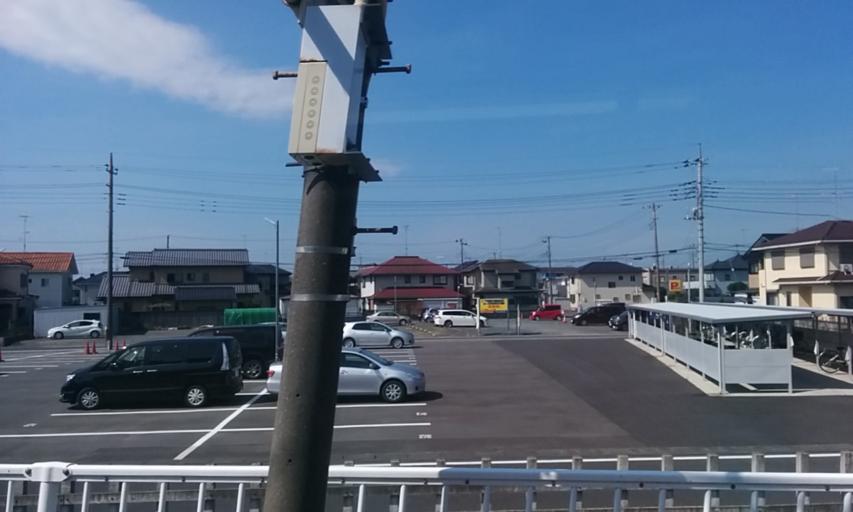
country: JP
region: Saitama
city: Hanyu
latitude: 36.1495
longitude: 139.5571
